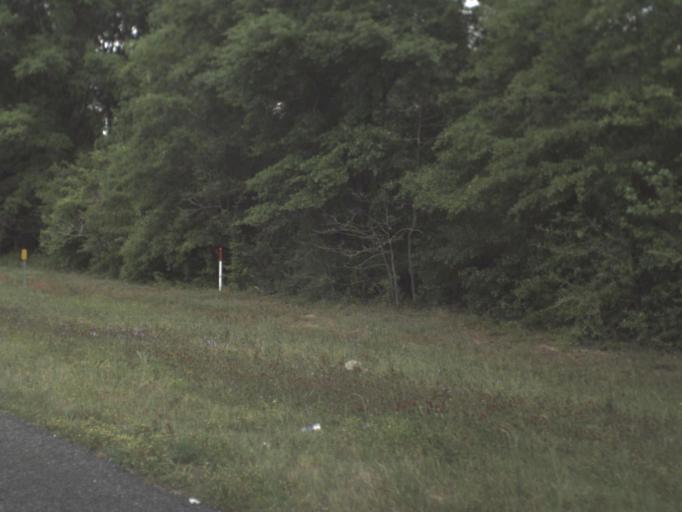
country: US
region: Florida
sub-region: Escambia County
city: Molino
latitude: 30.7432
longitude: -87.3482
